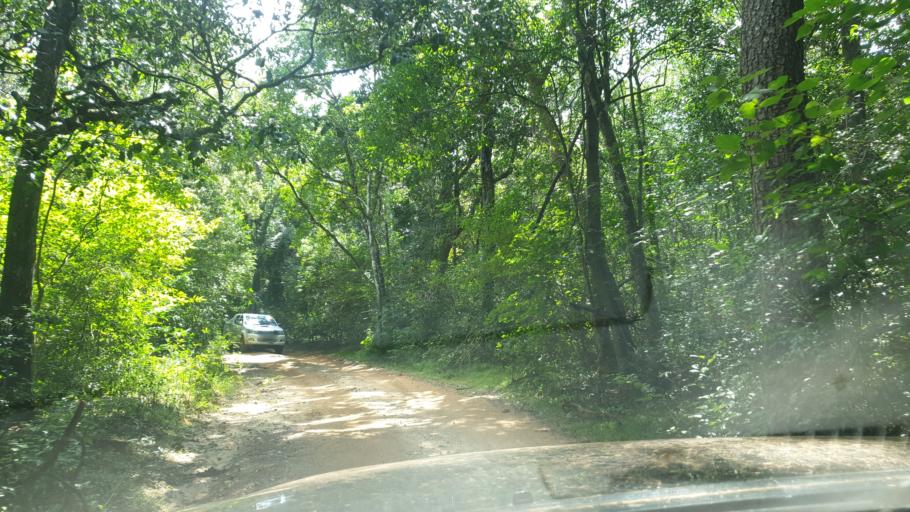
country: LK
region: North Central
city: Anuradhapura
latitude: 8.4226
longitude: 80.0235
